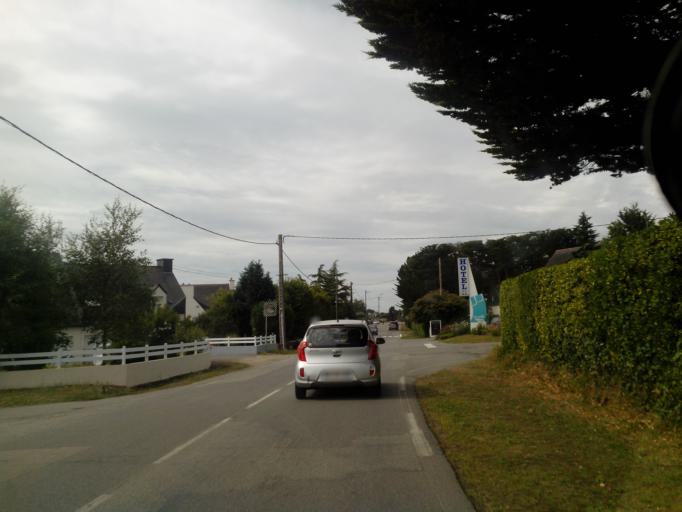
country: FR
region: Brittany
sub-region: Departement du Morbihan
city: Erdeven
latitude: 47.6301
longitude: -3.1582
